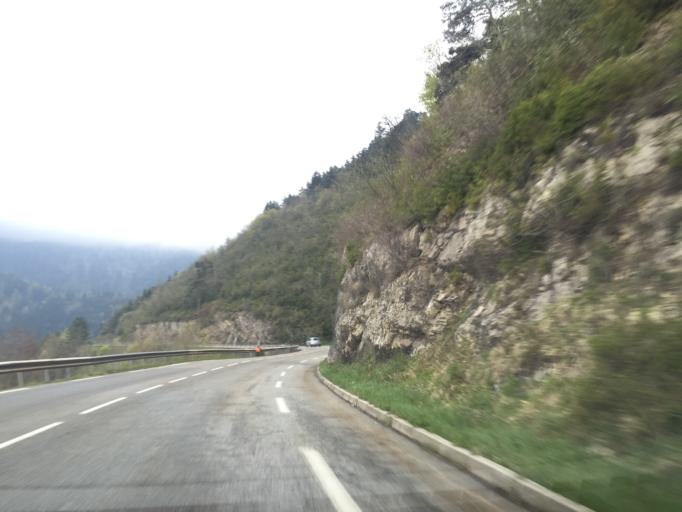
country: FR
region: Rhone-Alpes
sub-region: Departement de l'Isere
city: Mens
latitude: 44.7473
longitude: 5.6785
